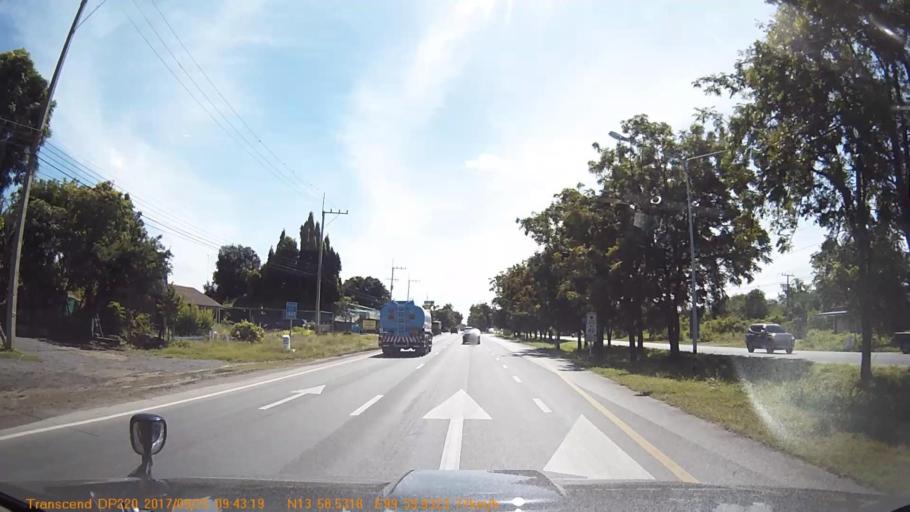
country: TH
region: Kanchanaburi
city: Tha Muang
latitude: 13.9755
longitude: 99.6656
